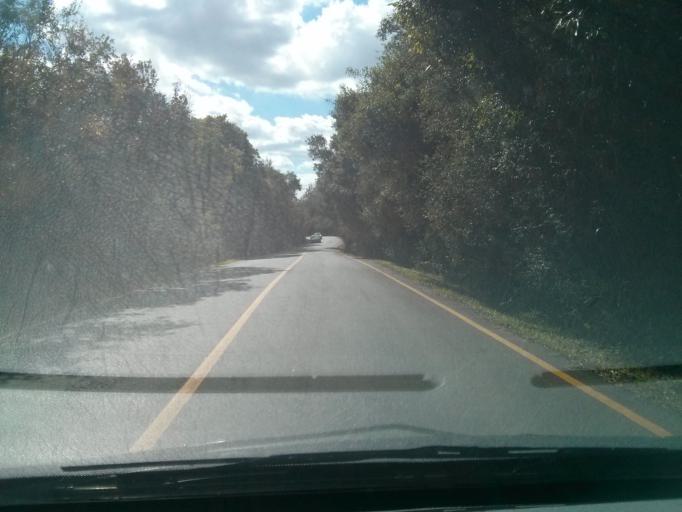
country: BR
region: Parana
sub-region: Sao Jose Dos Pinhais
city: Sao Jose dos Pinhais
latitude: -25.5490
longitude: -49.2241
